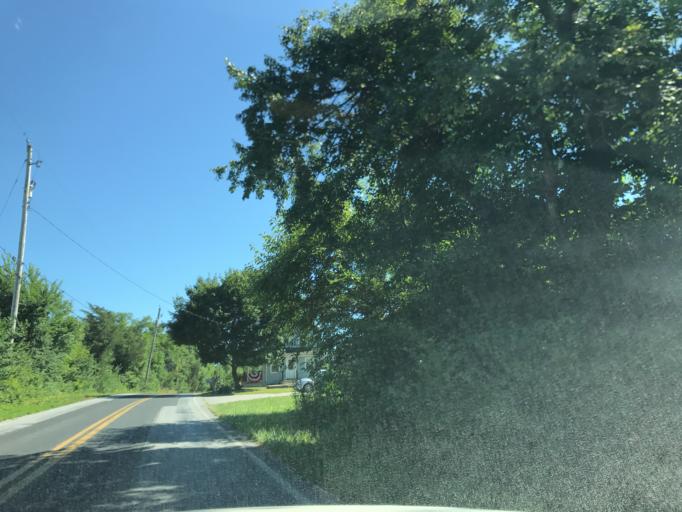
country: US
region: Pennsylvania
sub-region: York County
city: Pennville
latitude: 39.7729
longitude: -77.0062
